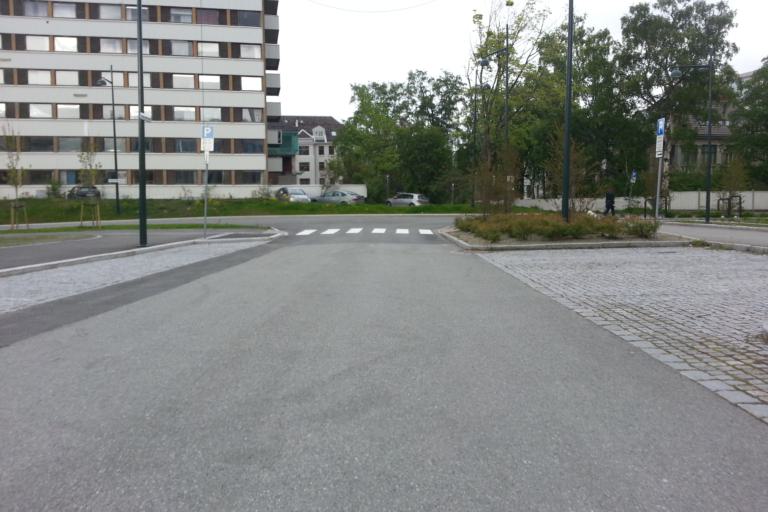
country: NO
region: Sor-Trondelag
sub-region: Trondheim
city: Trondheim
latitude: 63.4216
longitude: 10.3888
